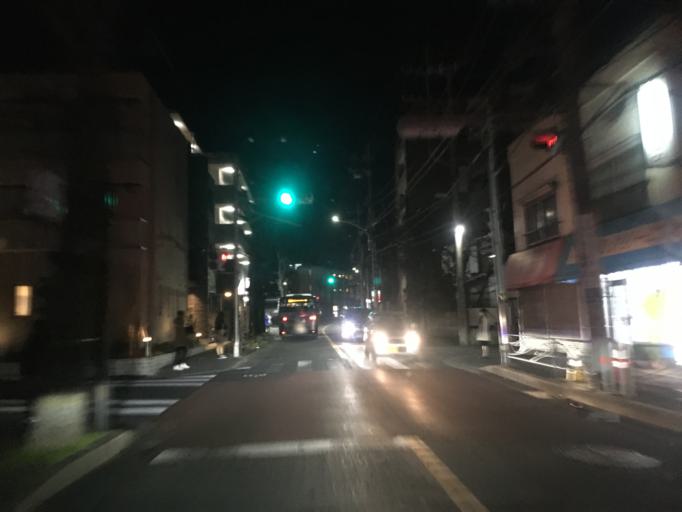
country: JP
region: Tokyo
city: Chofugaoka
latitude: 35.6148
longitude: 139.5227
